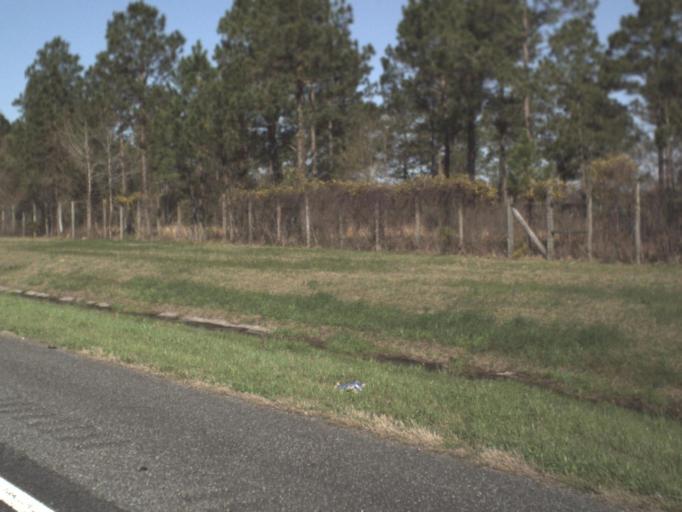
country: US
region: Florida
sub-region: Jefferson County
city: Monticello
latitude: 30.4782
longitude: -84.0694
